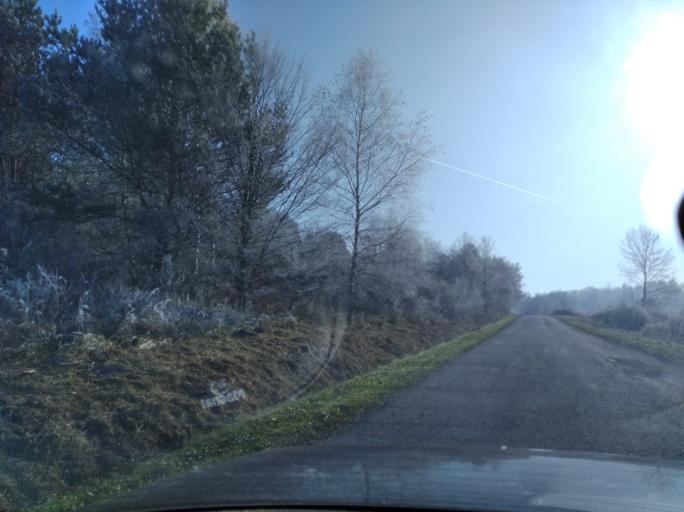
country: PL
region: Subcarpathian Voivodeship
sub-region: Powiat strzyzowski
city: Wysoka Strzyzowska
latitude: 49.8432
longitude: 21.7056
